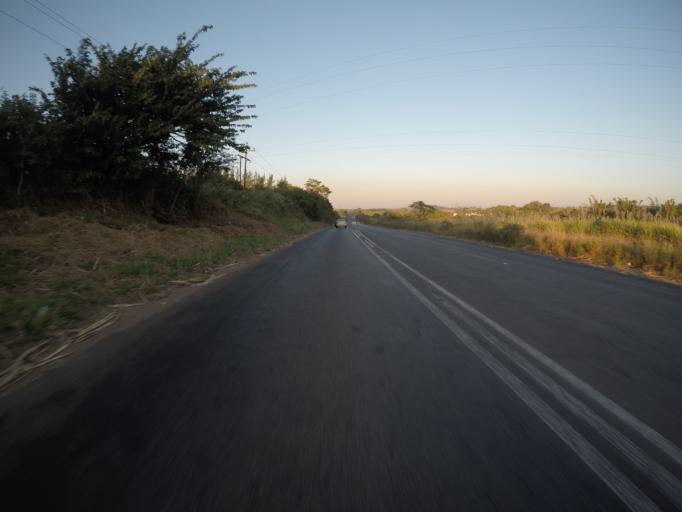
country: ZA
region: KwaZulu-Natal
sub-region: uThungulu District Municipality
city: Empangeni
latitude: -28.8129
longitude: 31.8903
